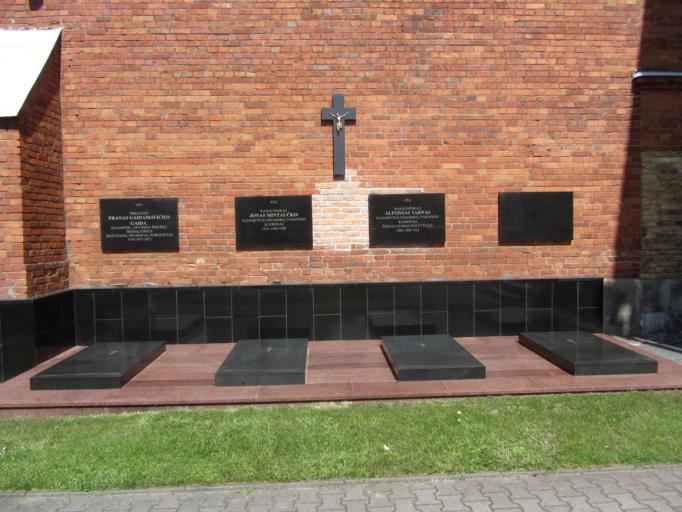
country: LT
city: Kaisiadorys
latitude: 54.8604
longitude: 24.4574
